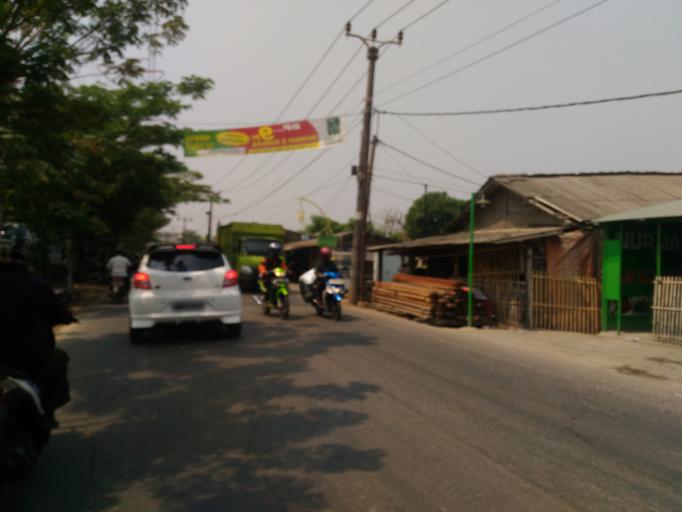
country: ID
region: West Java
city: Sepatan
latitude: -6.1480
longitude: 106.5808
